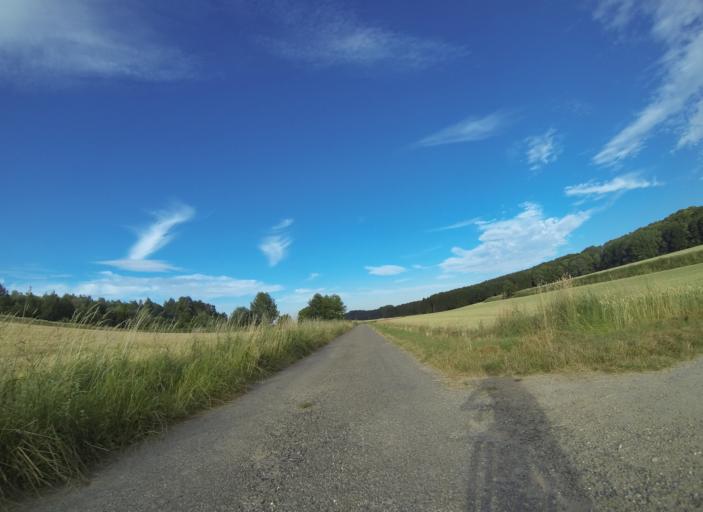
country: DE
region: Baden-Wuerttemberg
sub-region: Tuebingen Region
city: Altheim
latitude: 48.3257
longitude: 9.7880
